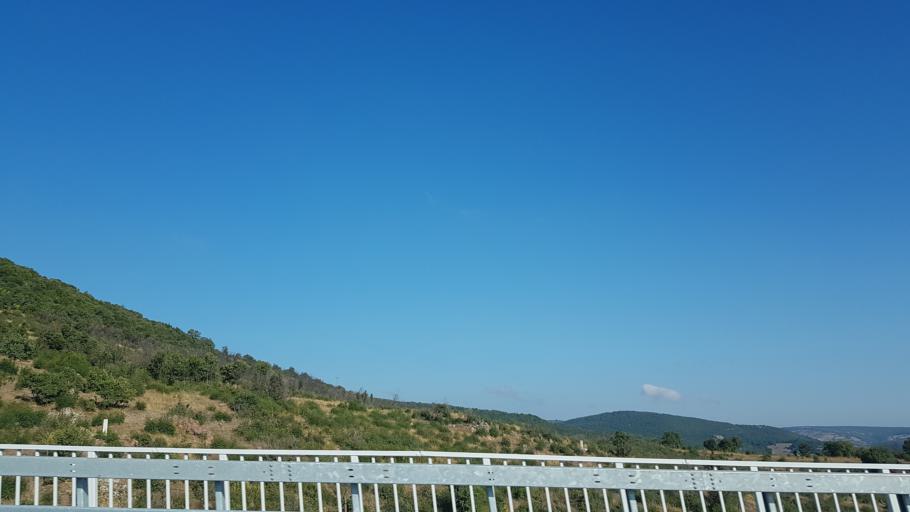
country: TR
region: Balikesir
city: Ertugrul
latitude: 39.5556
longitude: 27.6974
